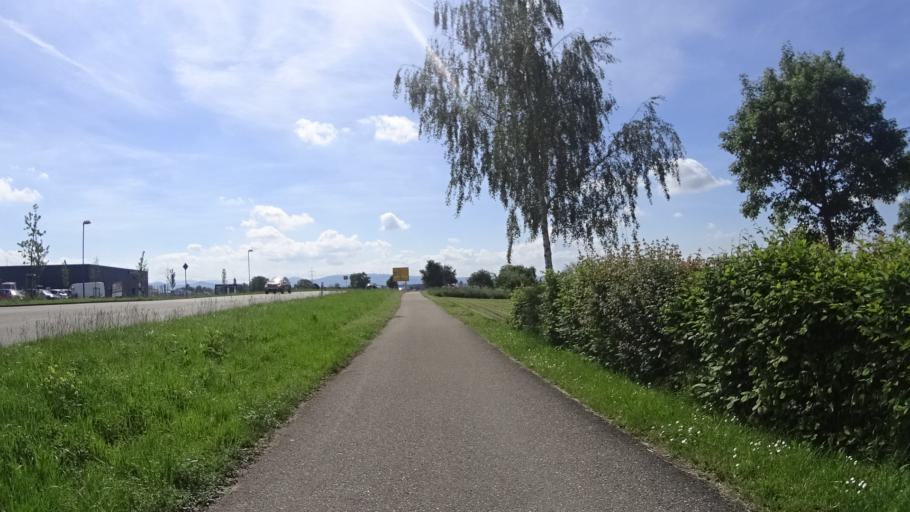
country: DE
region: Baden-Wuerttemberg
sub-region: Freiburg Region
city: Meissenheim
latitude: 48.4599
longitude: 7.8167
